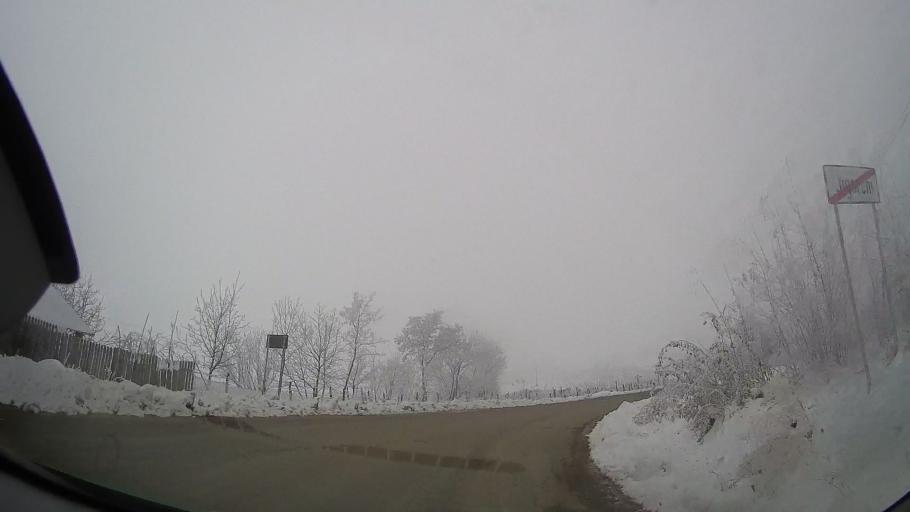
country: RO
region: Iasi
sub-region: Comuna Tibanesti
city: Tibanesti
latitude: 46.8935
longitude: 27.3077
